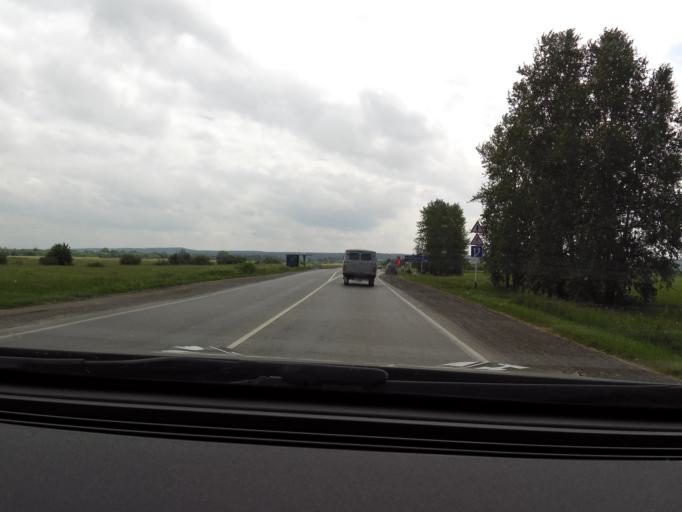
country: RU
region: Perm
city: Kukushtan
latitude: 57.5064
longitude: 56.6489
